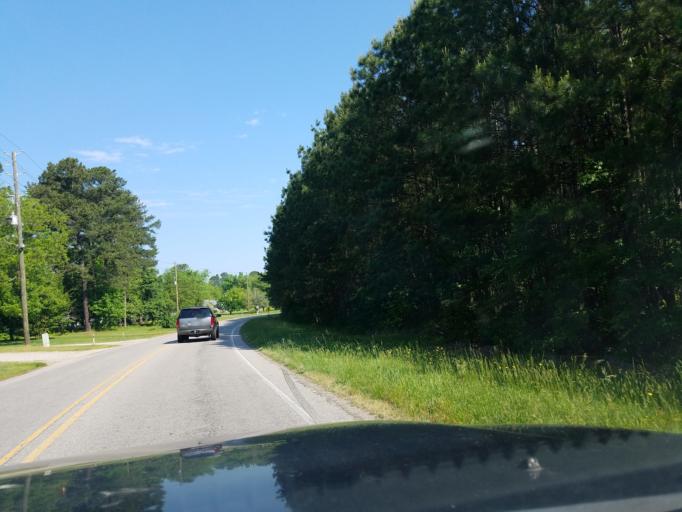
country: US
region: North Carolina
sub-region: Vance County
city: Henderson
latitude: 36.3392
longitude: -78.4461
